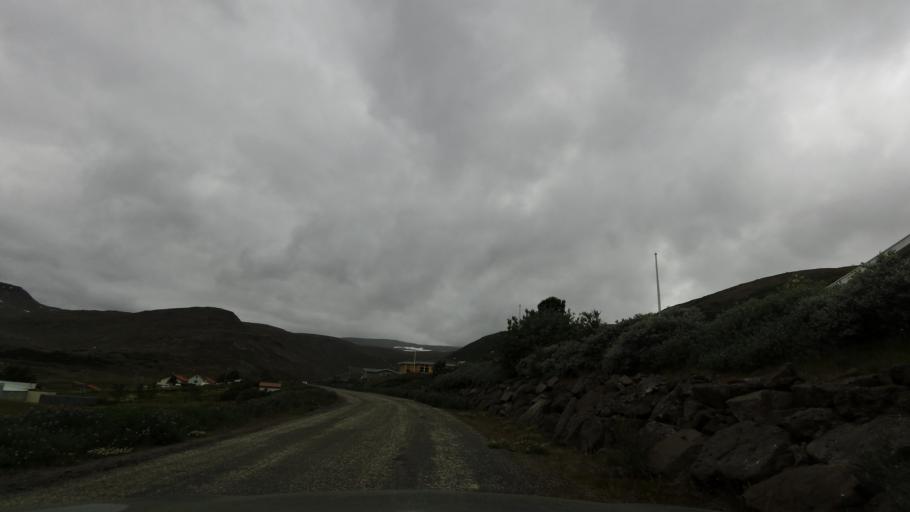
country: IS
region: Westfjords
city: Isafjoerdur
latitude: 66.0634
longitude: -23.1771
